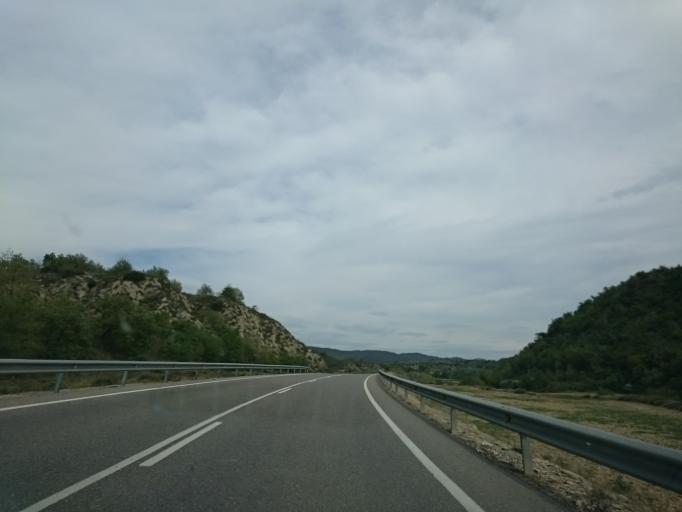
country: ES
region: Catalonia
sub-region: Provincia de Lleida
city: Tora de Riubregos
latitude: 41.8278
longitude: 1.3324
